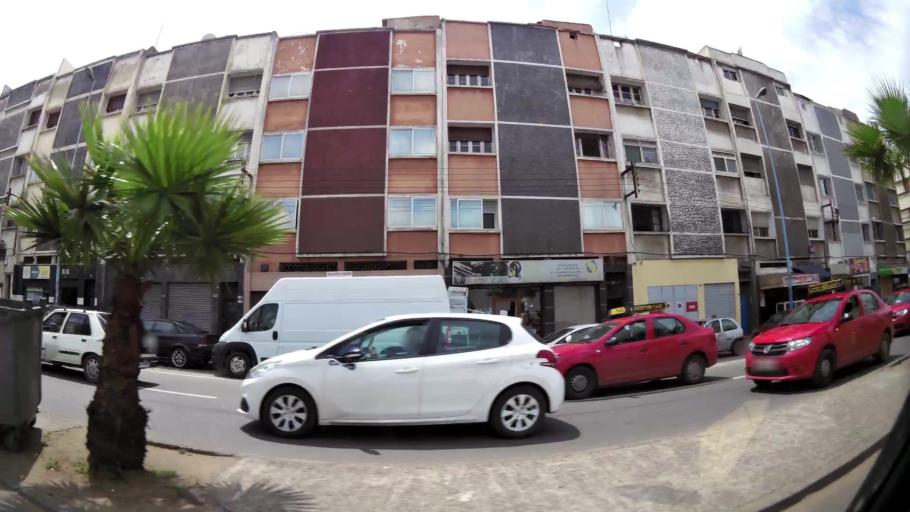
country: MA
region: Grand Casablanca
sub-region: Casablanca
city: Casablanca
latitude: 33.5845
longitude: -7.5728
